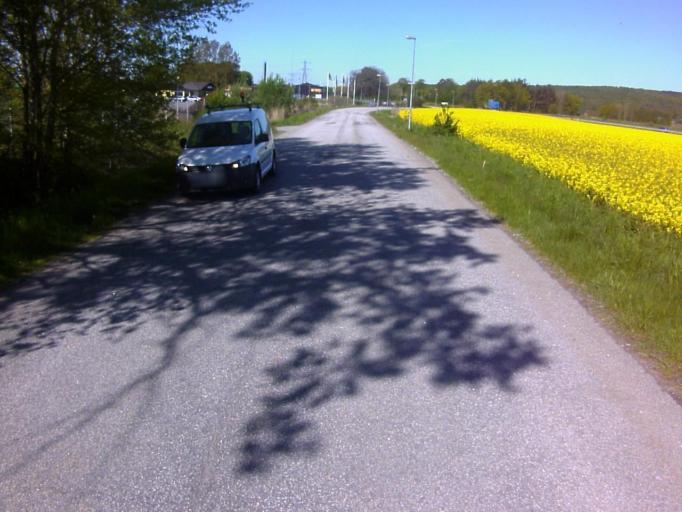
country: SE
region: Blekinge
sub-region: Solvesborgs Kommun
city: Soelvesborg
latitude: 56.0668
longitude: 14.6306
